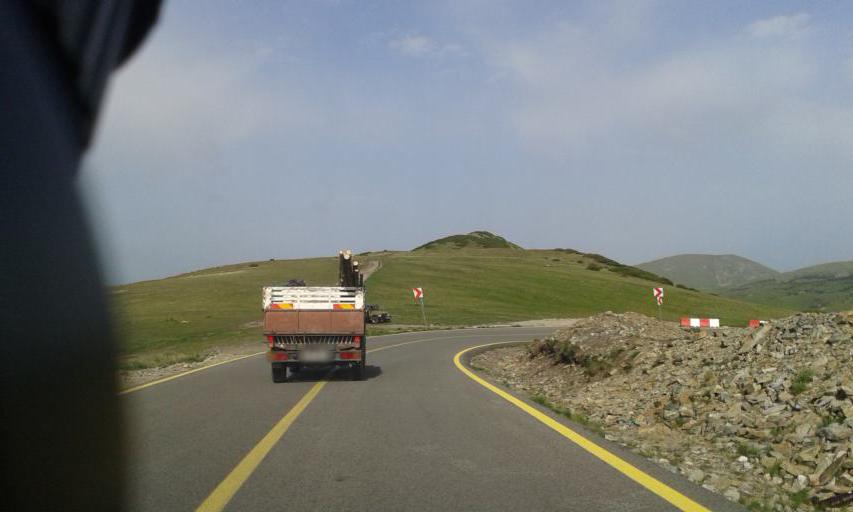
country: RO
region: Gorj
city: Novaci-Straini
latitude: 45.3584
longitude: 23.6686
